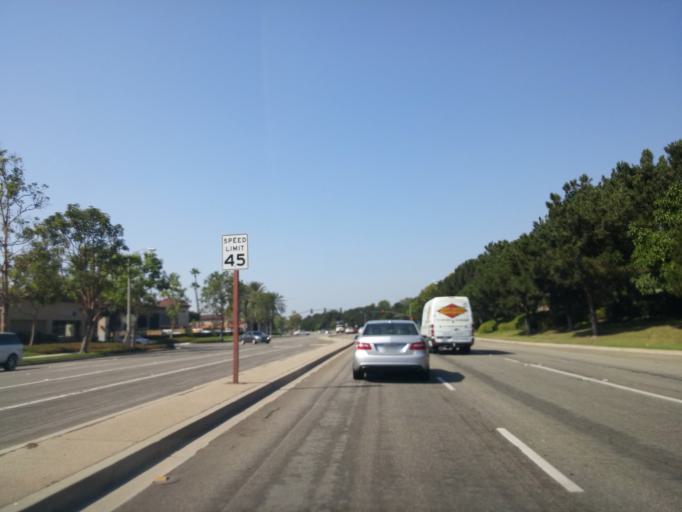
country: US
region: California
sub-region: Orange County
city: Irvine
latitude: 33.6848
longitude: -117.8091
